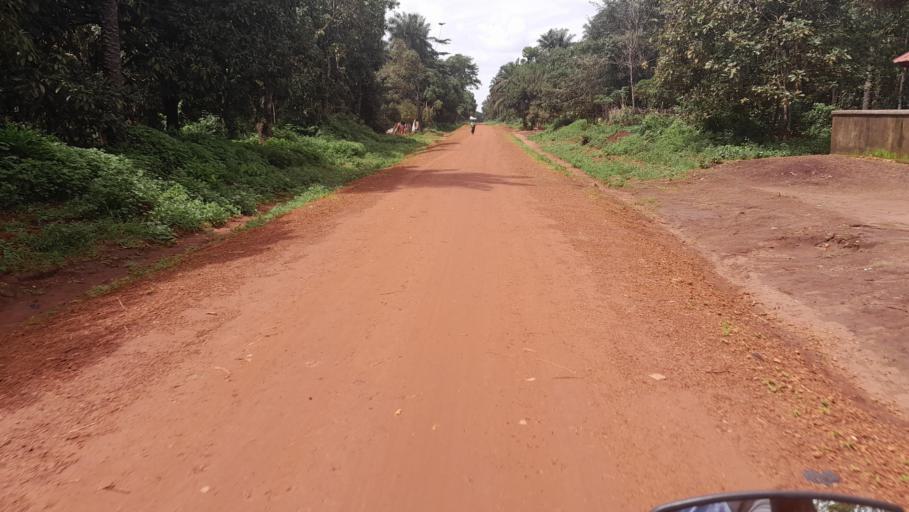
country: GN
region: Boke
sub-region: Boffa
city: Boffa
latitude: 10.0186
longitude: -13.8891
